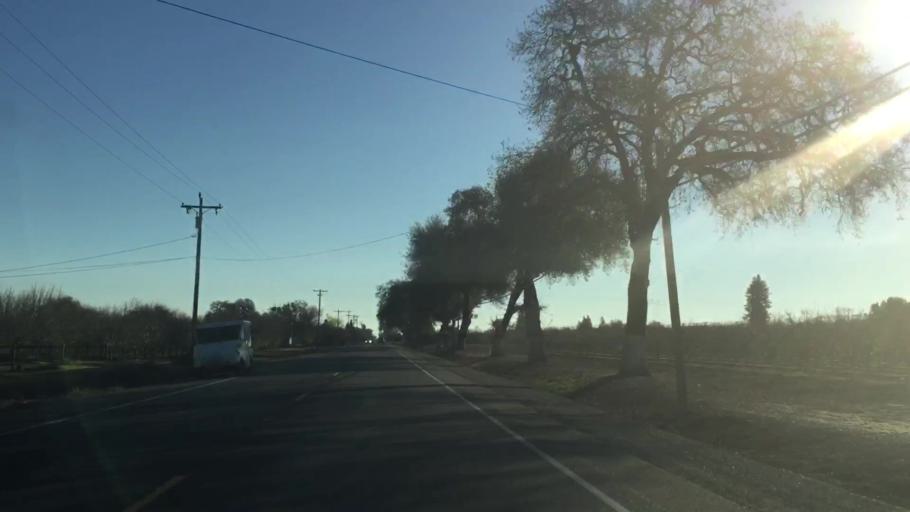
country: US
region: California
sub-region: Sutter County
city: Live Oak
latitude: 39.2461
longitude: -121.5995
